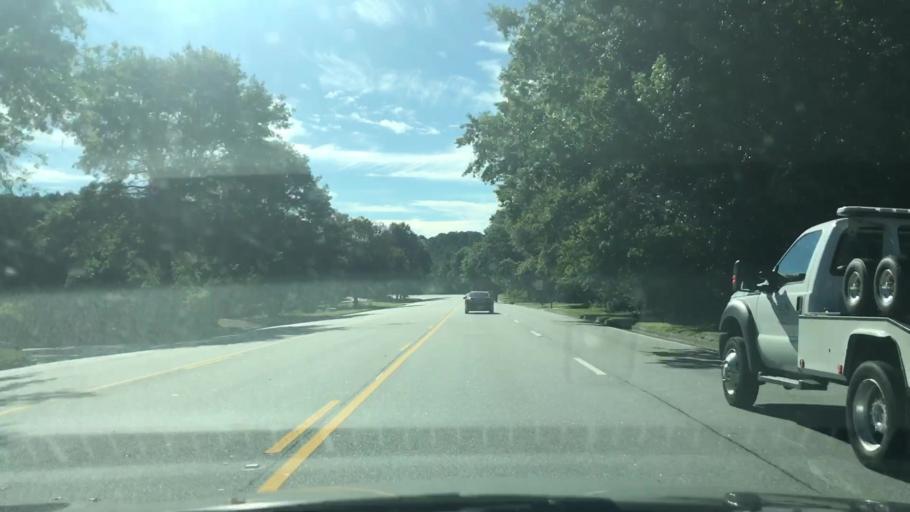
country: US
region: Georgia
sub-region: Gwinnett County
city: Mountain Park
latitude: 33.8160
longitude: -84.1166
